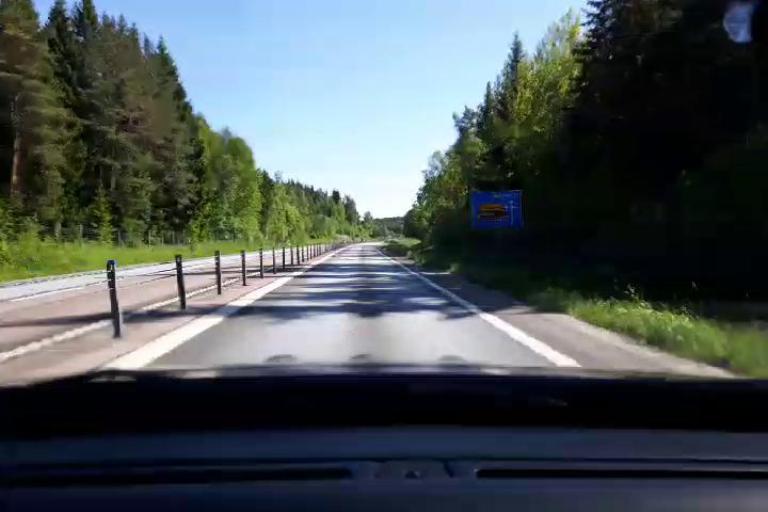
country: SE
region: Gaevleborg
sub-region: Soderhamns Kommun
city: Soderhamn
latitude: 61.2846
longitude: 17.0255
